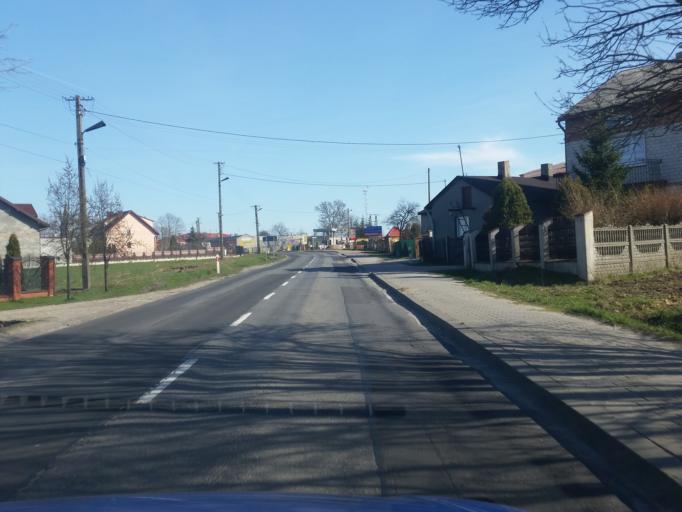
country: PL
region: Lodz Voivodeship
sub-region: Powiat radomszczanski
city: Kamiensk
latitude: 51.2066
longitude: 19.4930
